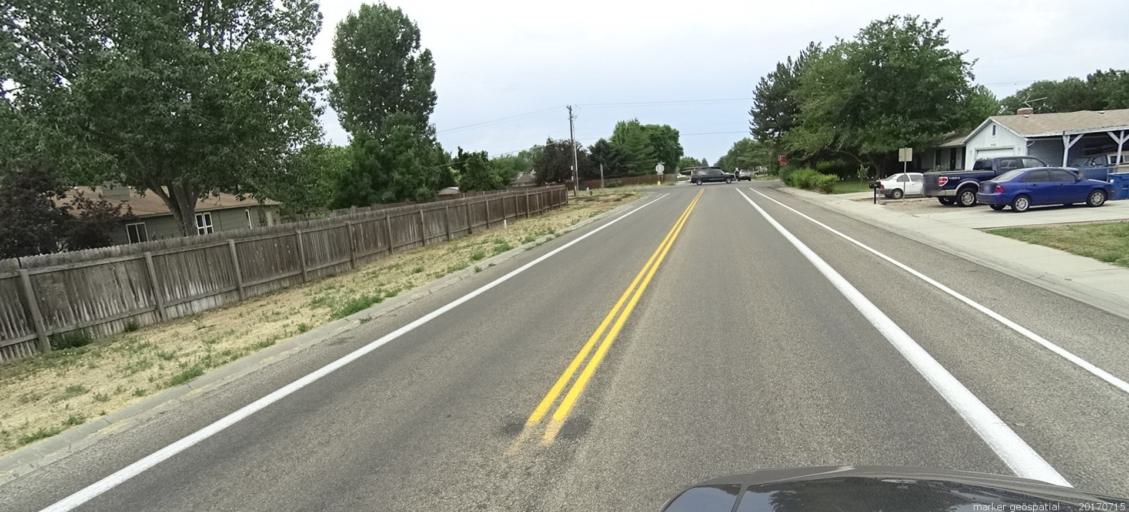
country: US
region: Idaho
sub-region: Ada County
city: Garden City
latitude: 43.5538
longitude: -116.2933
